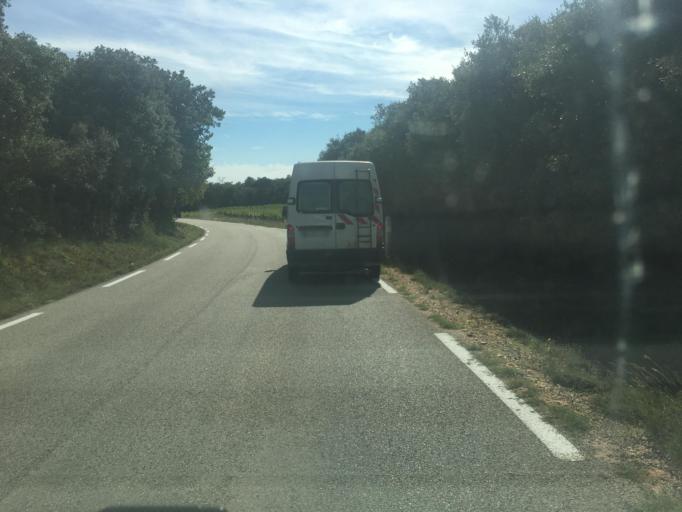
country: FR
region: Languedoc-Roussillon
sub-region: Departement du Gard
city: Connaux
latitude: 44.0488
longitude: 4.5676
